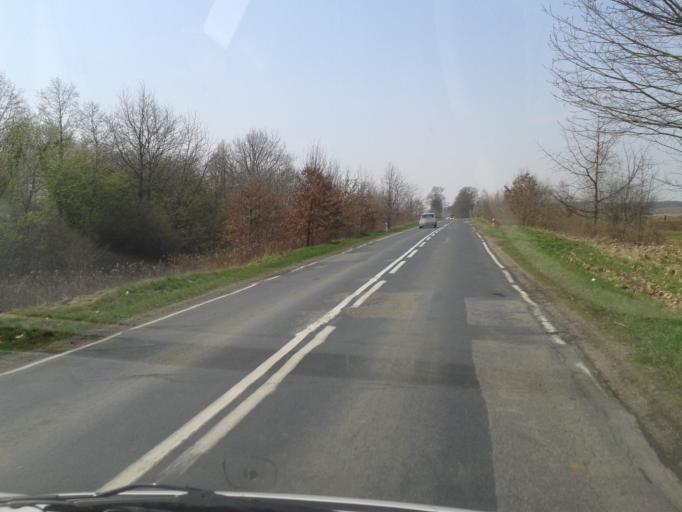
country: PL
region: Subcarpathian Voivodeship
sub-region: Powiat jaroslawski
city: Wiazownica
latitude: 50.0650
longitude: 22.8031
